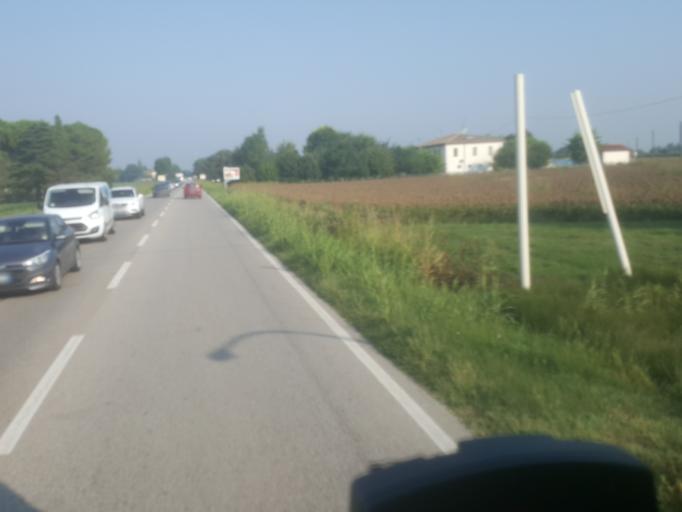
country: IT
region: Emilia-Romagna
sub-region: Provincia di Ravenna
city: Fornace Zarattini
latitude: 44.4395
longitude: 12.1396
